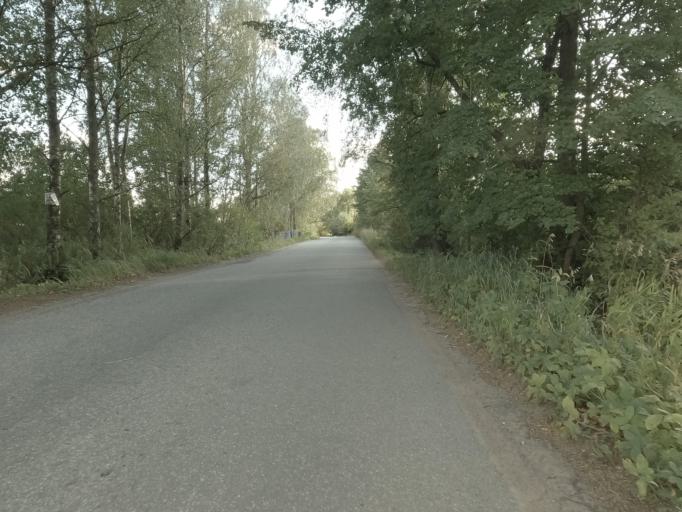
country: RU
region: Leningrad
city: Ul'yanovka
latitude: 59.6293
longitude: 30.7936
